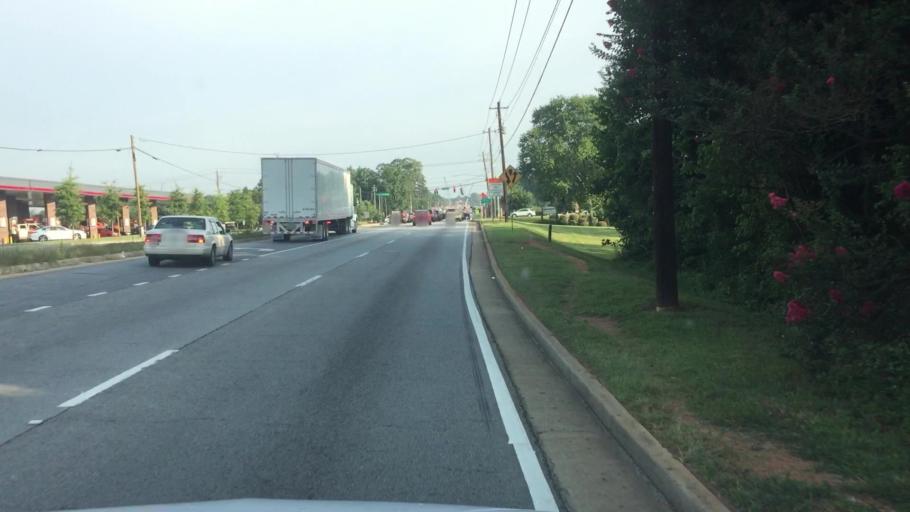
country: US
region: Georgia
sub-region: DeKalb County
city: Panthersville
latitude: 33.6917
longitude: -84.2594
